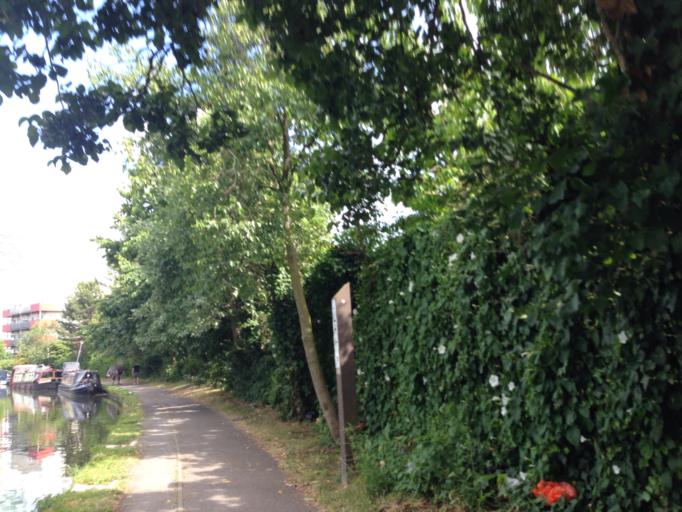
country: GB
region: England
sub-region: Greater London
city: Wembley
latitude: 51.5396
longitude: -0.3044
